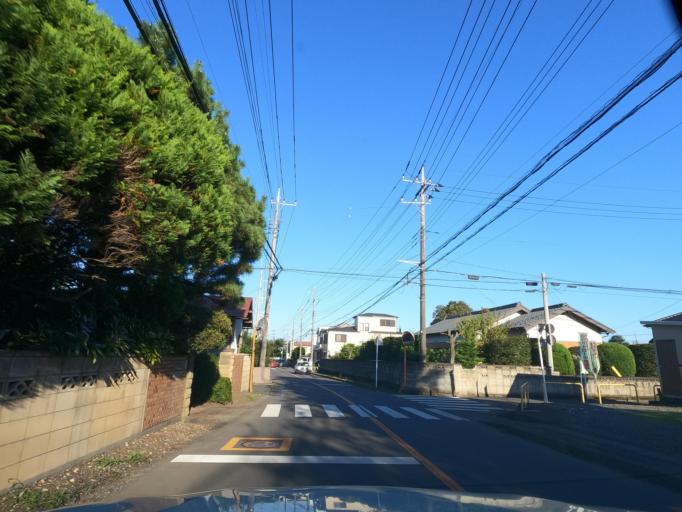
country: JP
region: Saitama
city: Hanno
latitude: 35.8680
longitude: 139.3492
